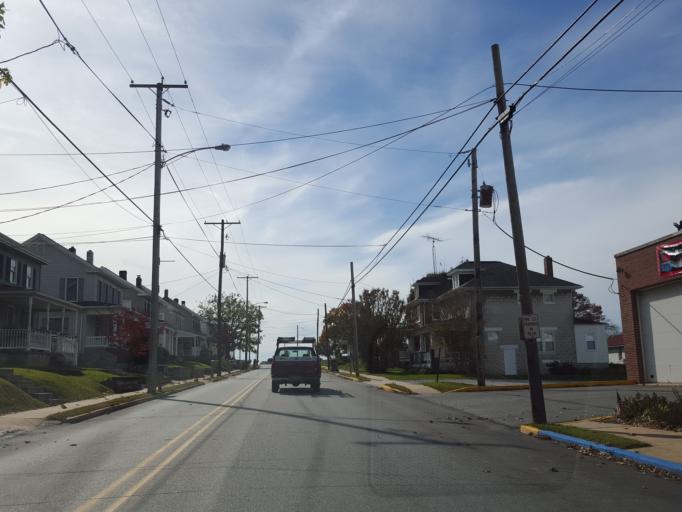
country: US
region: Pennsylvania
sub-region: York County
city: Hallam
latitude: 39.9761
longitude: -76.5844
